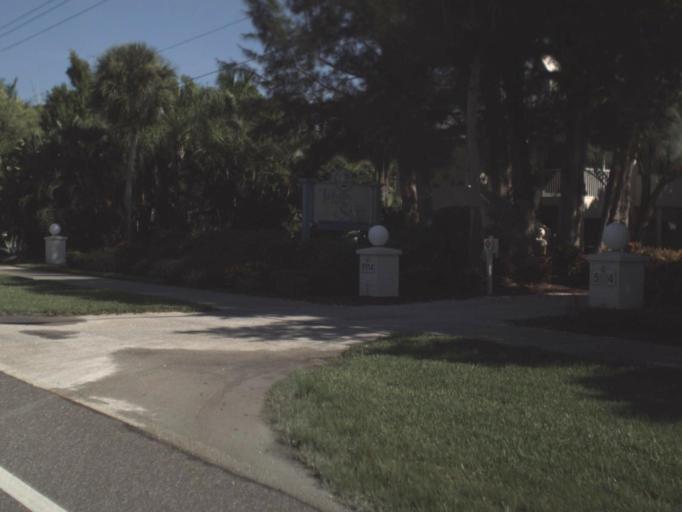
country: US
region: Florida
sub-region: Manatee County
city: Longboat Key
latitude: 27.4065
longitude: -82.6532
